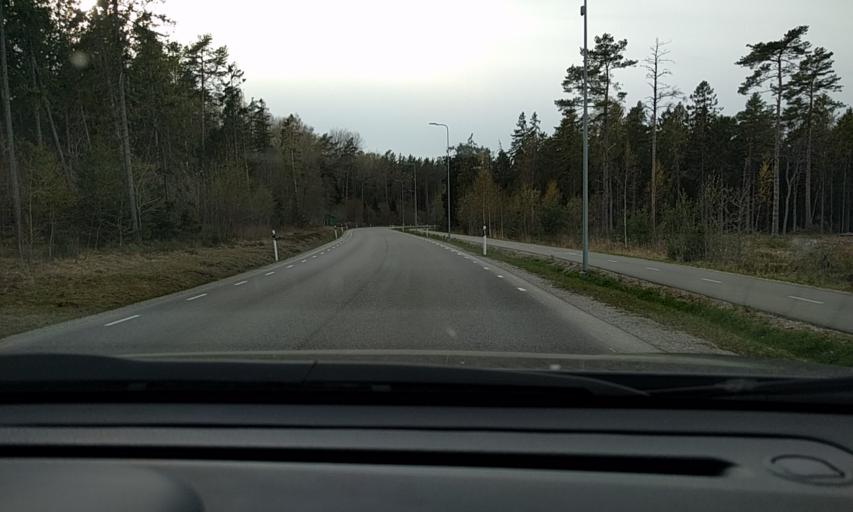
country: EE
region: Harju
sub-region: Viimsi vald
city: Viimsi
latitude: 59.5230
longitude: 24.8897
